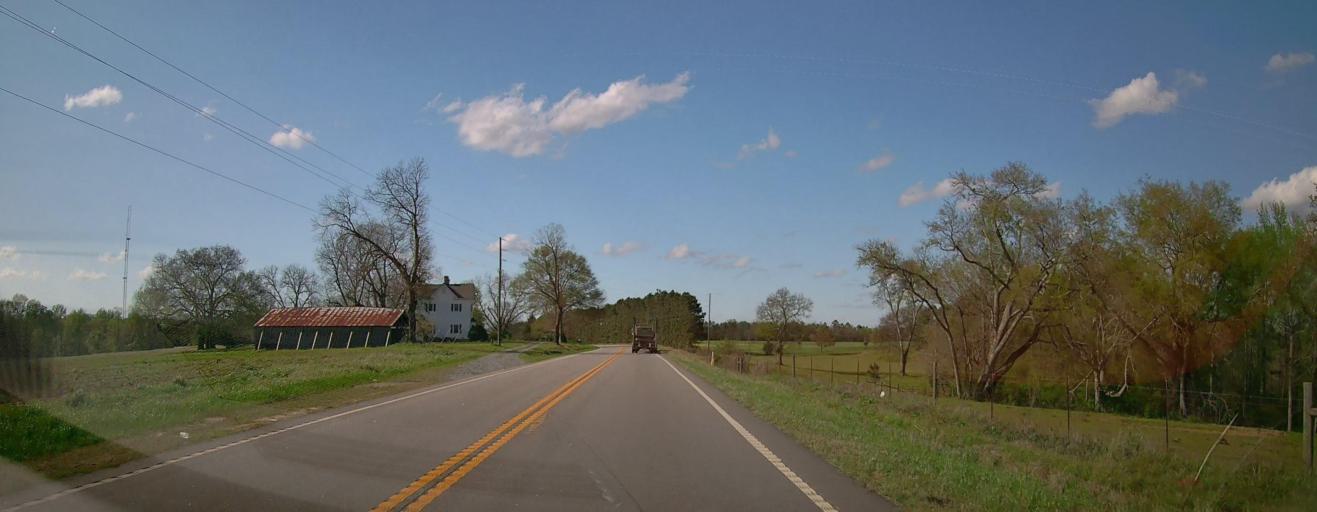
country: US
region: Georgia
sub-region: Baldwin County
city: Hardwick
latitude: 33.0722
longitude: -83.1365
